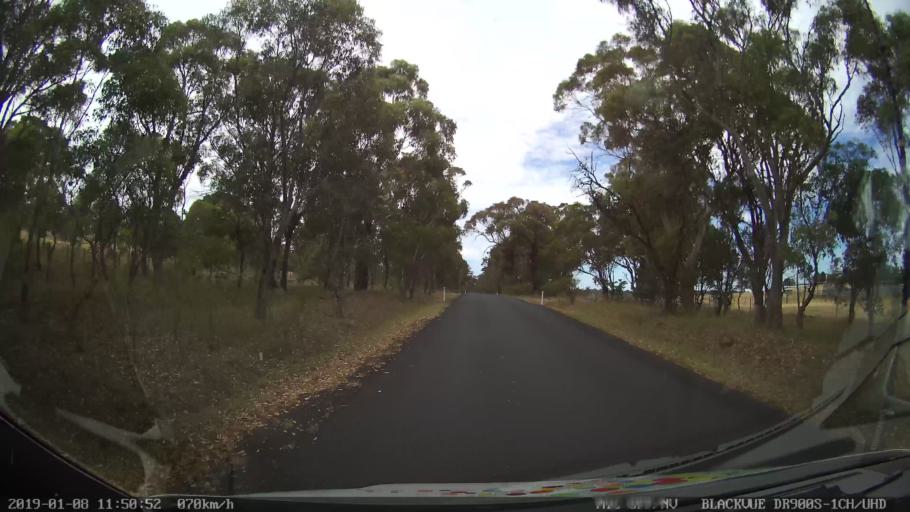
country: AU
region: New South Wales
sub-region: Armidale Dumaresq
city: Armidale
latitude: -30.3872
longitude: 151.5578
